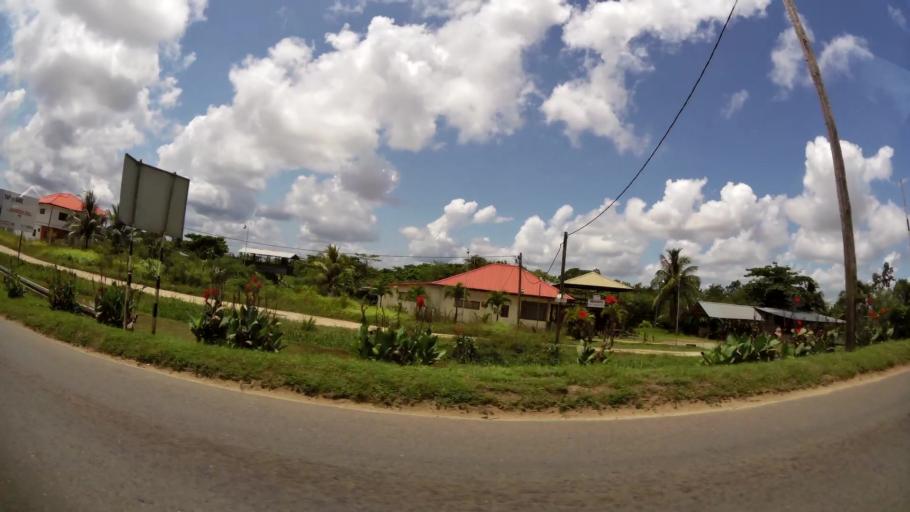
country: SR
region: Paramaribo
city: Paramaribo
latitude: 5.8071
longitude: -55.1566
